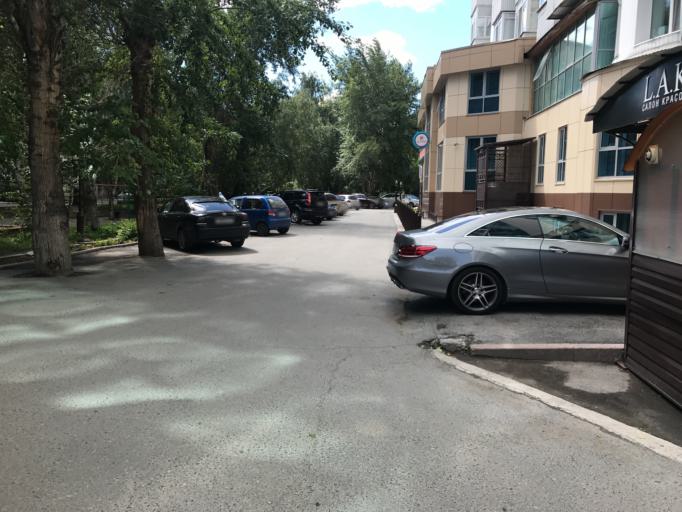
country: RU
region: Tjumen
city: Tyumen
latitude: 57.1492
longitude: 65.5331
